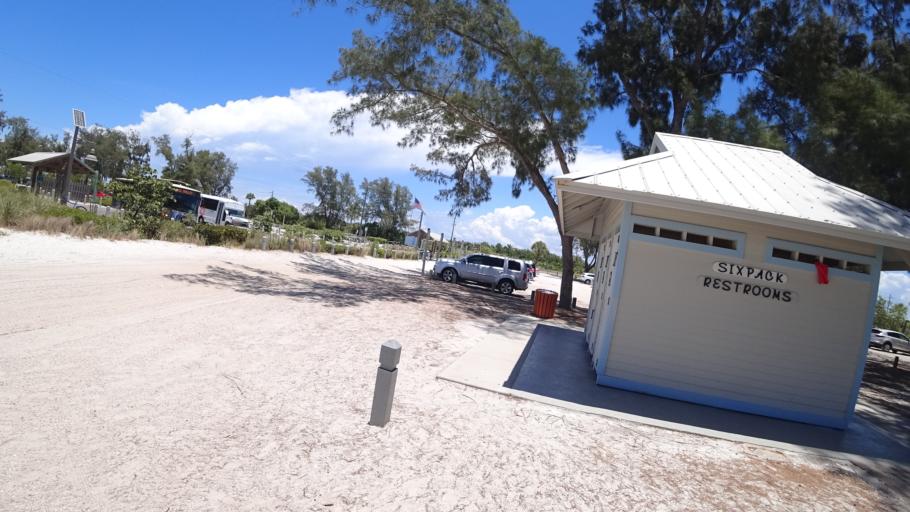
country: US
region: Florida
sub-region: Manatee County
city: Cortez
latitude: 27.4508
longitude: -82.6925
